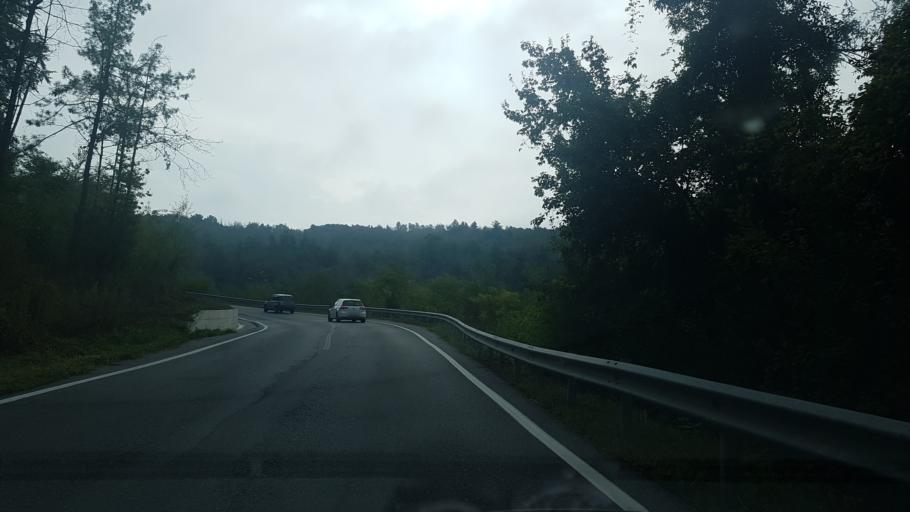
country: IT
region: Piedmont
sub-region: Provincia di Cuneo
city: Sale delle Langhe
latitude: 44.4007
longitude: 8.1076
